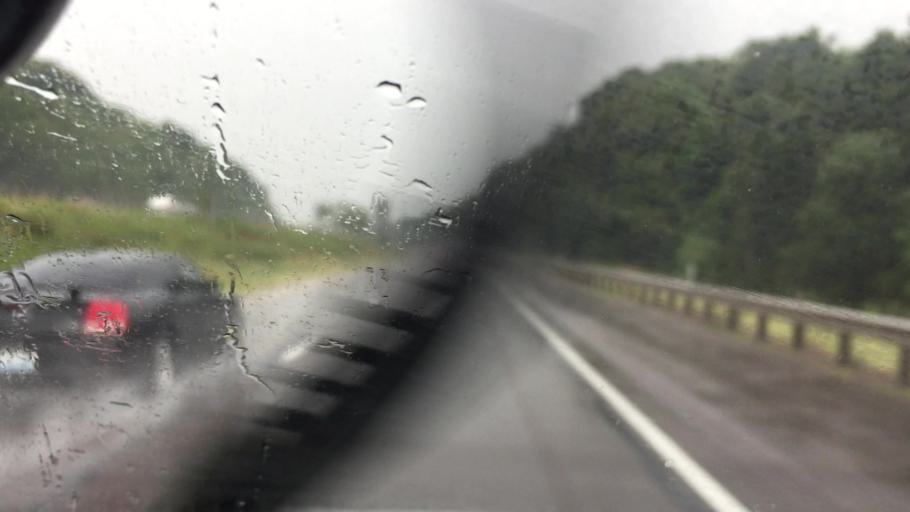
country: US
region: Maryland
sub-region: Garrett County
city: Oakland
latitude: 39.6873
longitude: -79.3538
